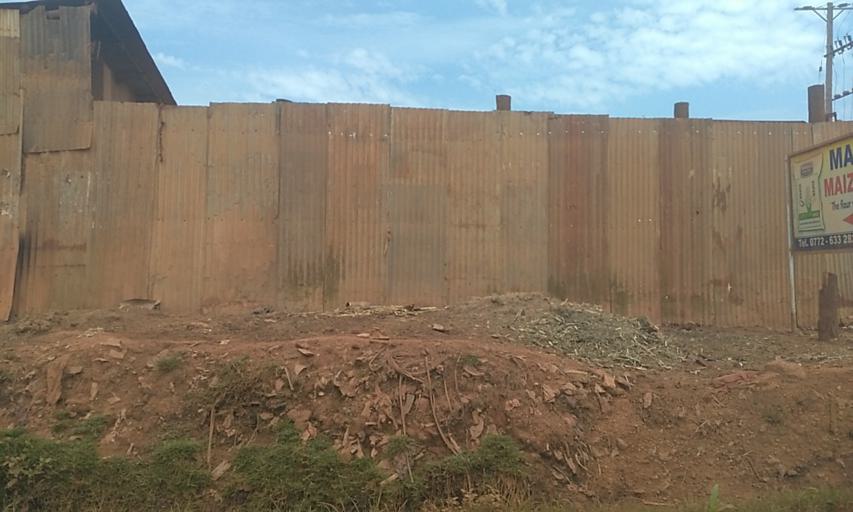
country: UG
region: Central Region
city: Kampala Central Division
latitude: 0.2962
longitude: 32.5237
